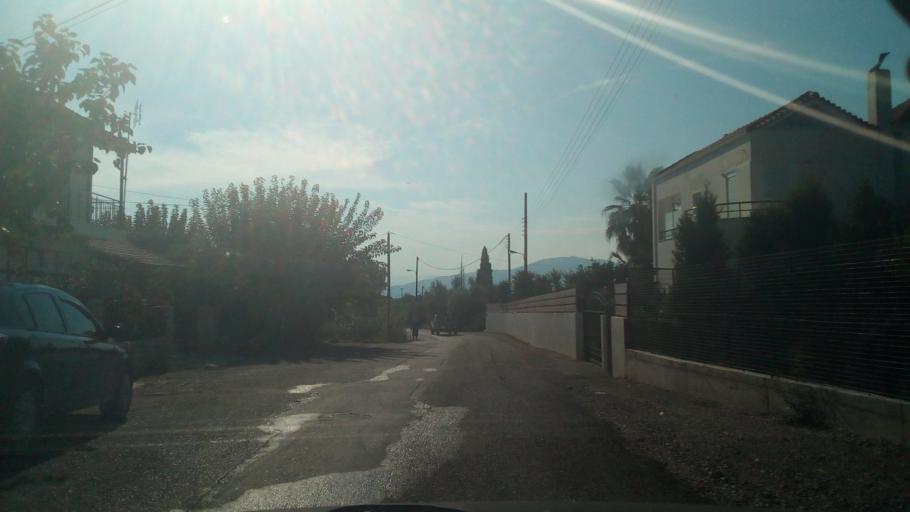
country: GR
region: West Greece
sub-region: Nomos Aitolias kai Akarnanias
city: Nafpaktos
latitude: 38.4040
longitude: 21.8542
